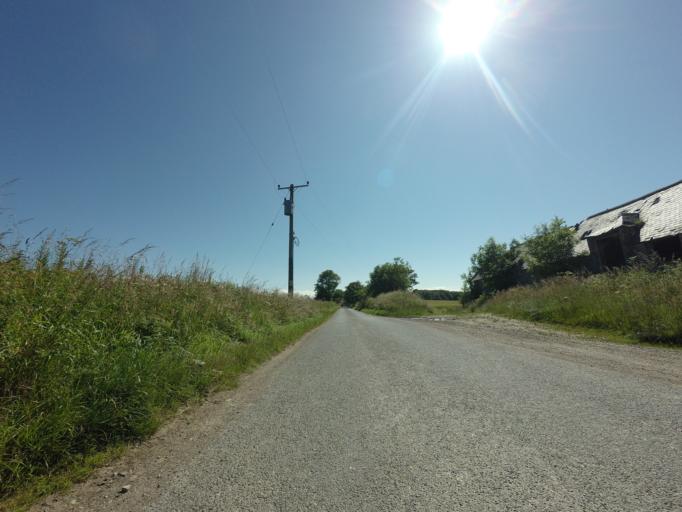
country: GB
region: Scotland
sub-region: Aberdeenshire
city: Macduff
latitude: 57.6539
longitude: -2.5011
